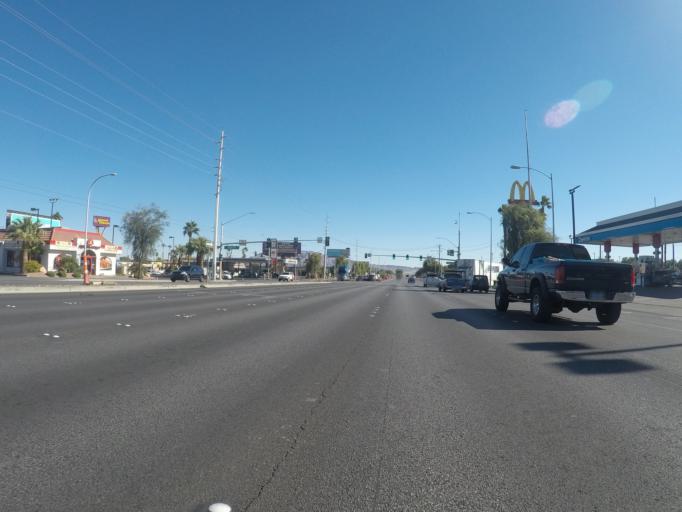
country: US
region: Nevada
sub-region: Clark County
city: Winchester
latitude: 36.1441
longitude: -115.1380
